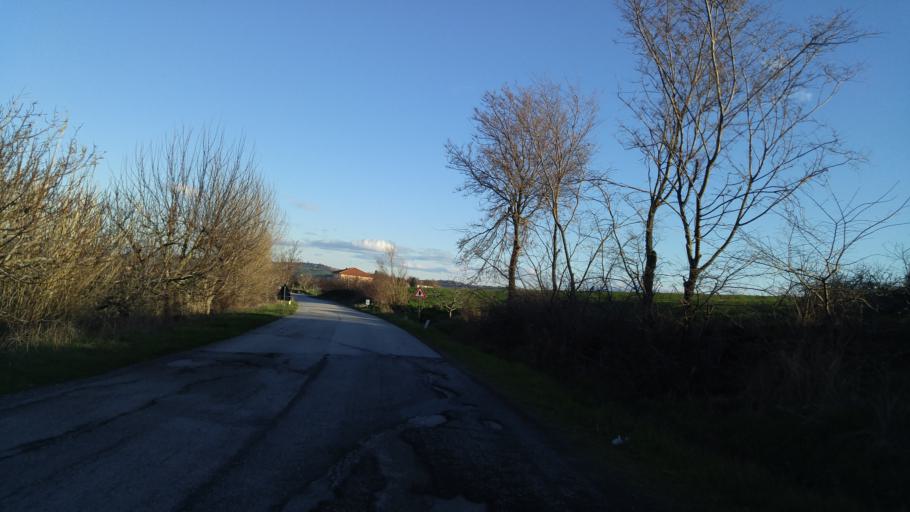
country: IT
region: The Marches
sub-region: Provincia di Pesaro e Urbino
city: Mondolfo
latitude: 43.7591
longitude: 13.1144
